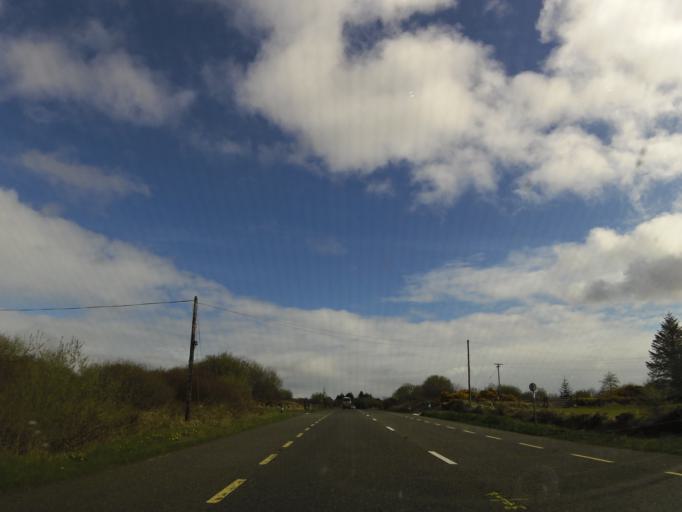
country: IE
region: Connaught
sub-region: Maigh Eo
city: Ballyhaunis
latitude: 53.9038
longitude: -8.7964
